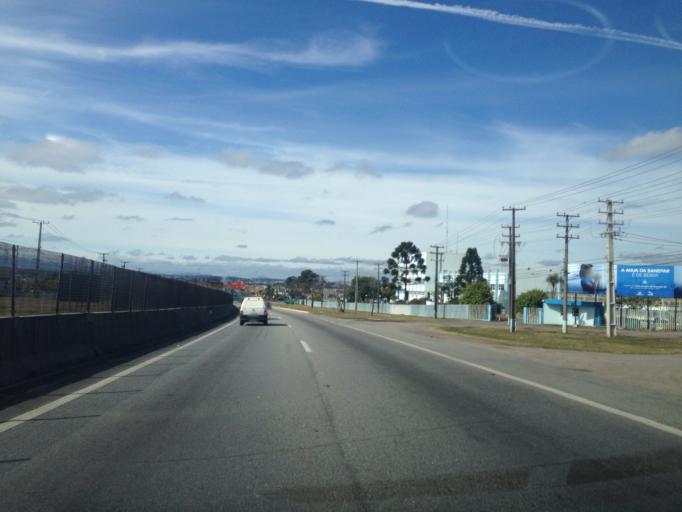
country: BR
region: Parana
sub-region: Pinhais
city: Pinhais
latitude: -25.4766
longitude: -49.2062
